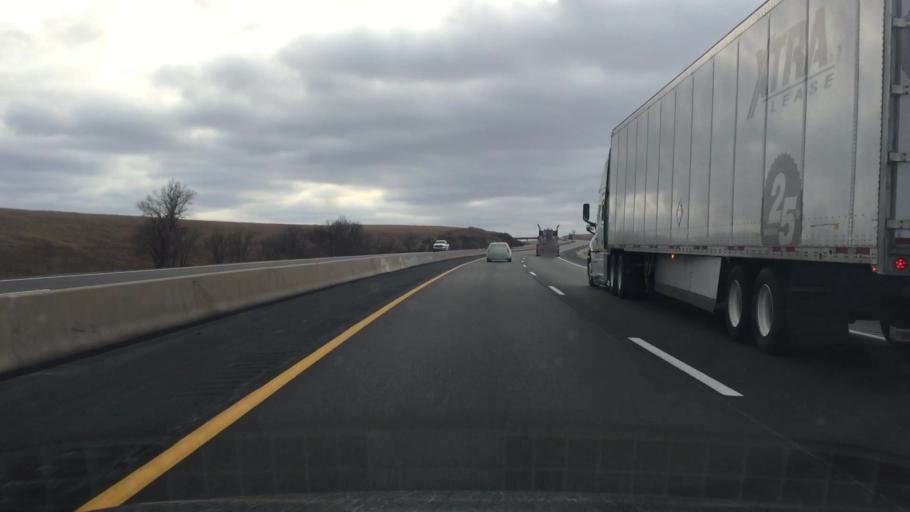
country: US
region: Kansas
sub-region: Chase County
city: Cottonwood Falls
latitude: 38.1690
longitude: -96.4764
